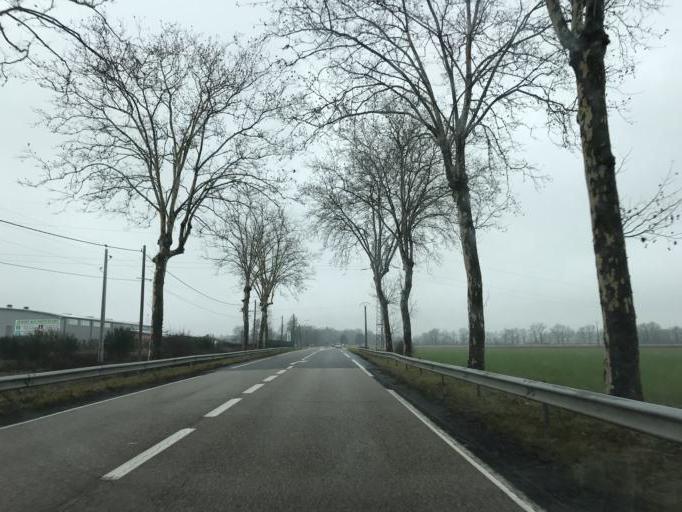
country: FR
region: Rhone-Alpes
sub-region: Departement de l'Ain
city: Servas
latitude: 46.1210
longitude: 5.1561
